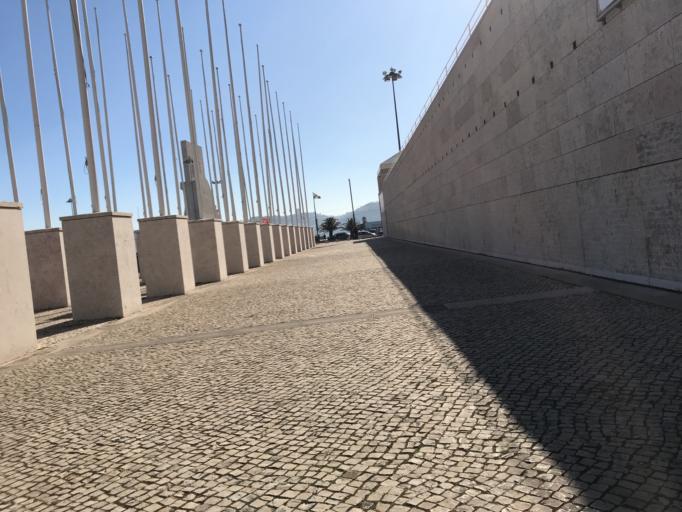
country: PT
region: Lisbon
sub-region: Oeiras
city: Alges
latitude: 38.6957
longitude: -9.2074
